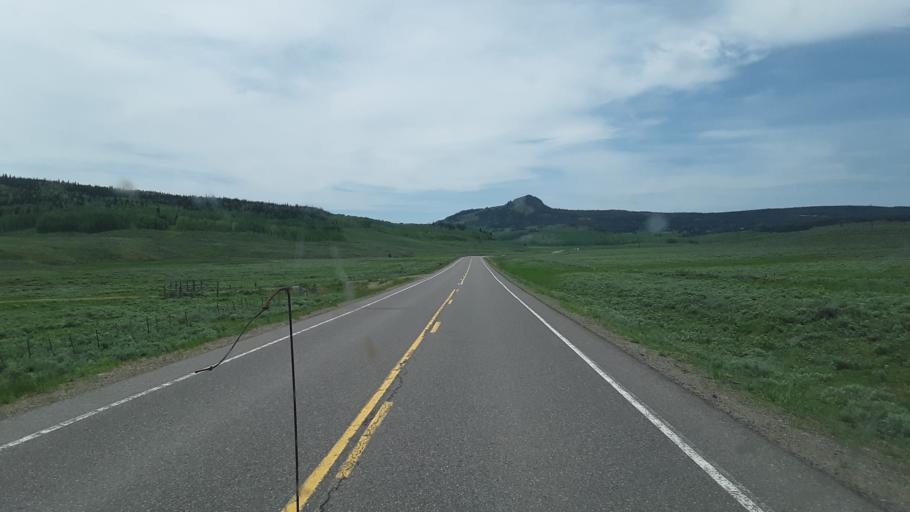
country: US
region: Colorado
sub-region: Routt County
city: Steamboat Springs
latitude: 40.3997
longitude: -106.5484
